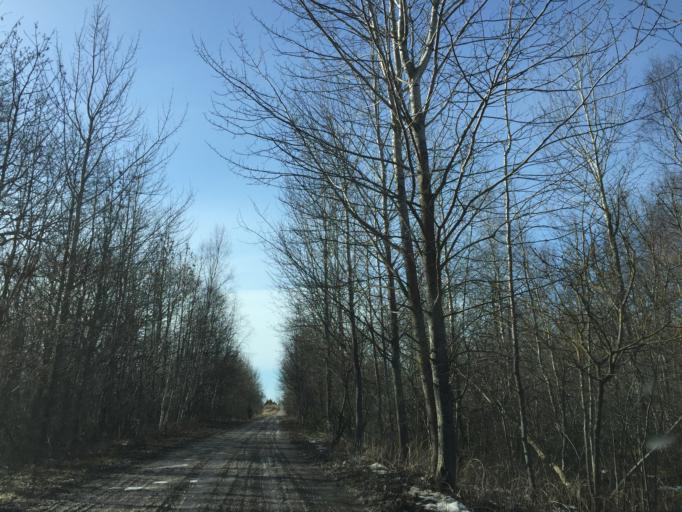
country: EE
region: Laeaene
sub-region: Haapsalu linn
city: Haapsalu
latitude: 58.6556
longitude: 23.5147
